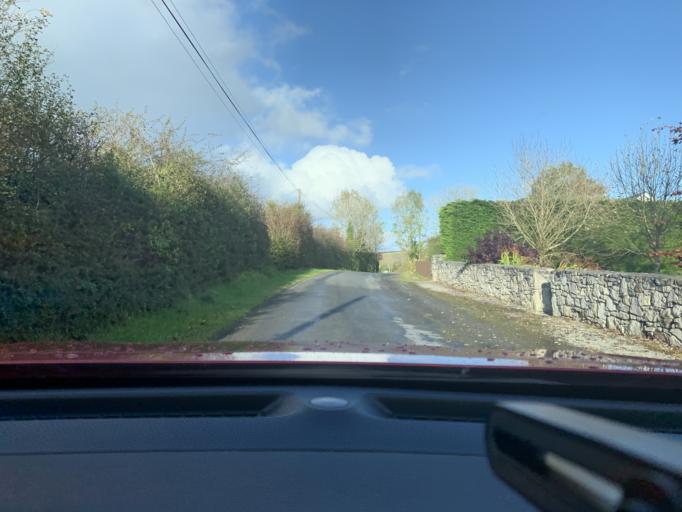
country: IE
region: Connaught
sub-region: Sligo
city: Ballymote
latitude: 54.1074
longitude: -8.4335
